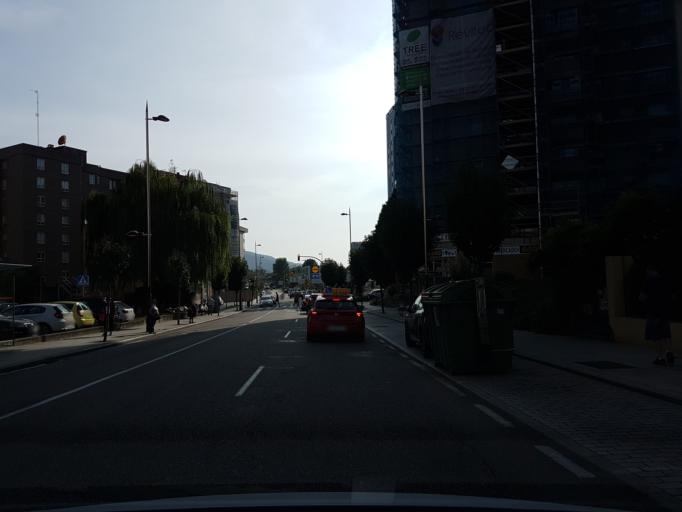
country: ES
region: Galicia
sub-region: Provincia de Pontevedra
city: Vigo
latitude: 42.2116
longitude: -8.7462
